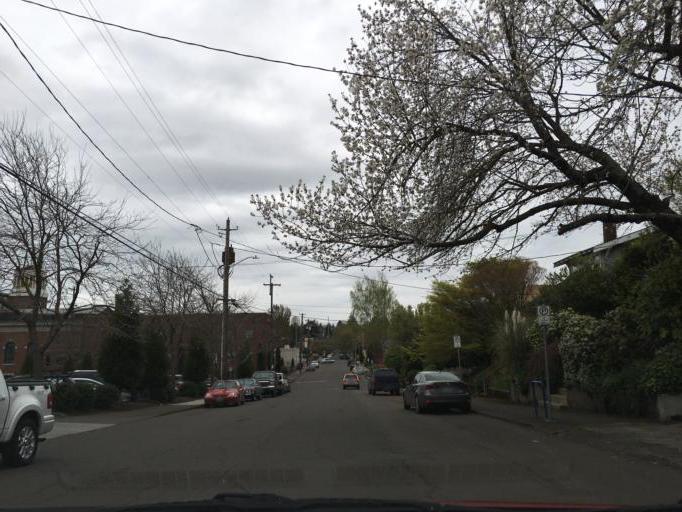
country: US
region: Oregon
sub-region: Multnomah County
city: Portland
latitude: 45.5358
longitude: -122.6170
